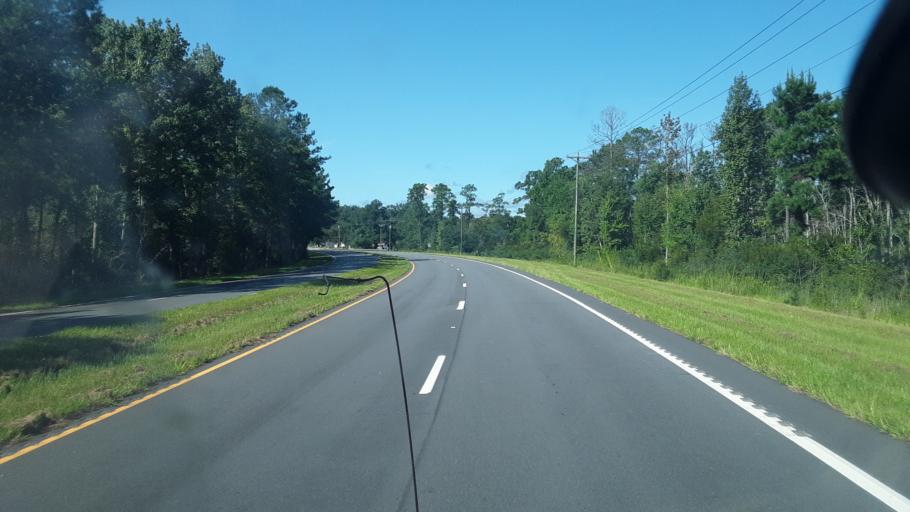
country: US
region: South Carolina
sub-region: Hampton County
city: Yemassee
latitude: 32.5913
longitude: -80.9243
